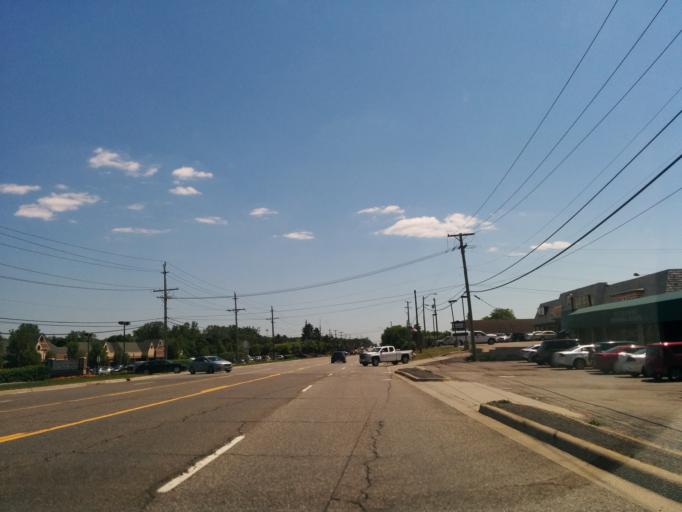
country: US
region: Michigan
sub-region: Oakland County
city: Orchard Lake
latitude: 42.5762
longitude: -83.3625
